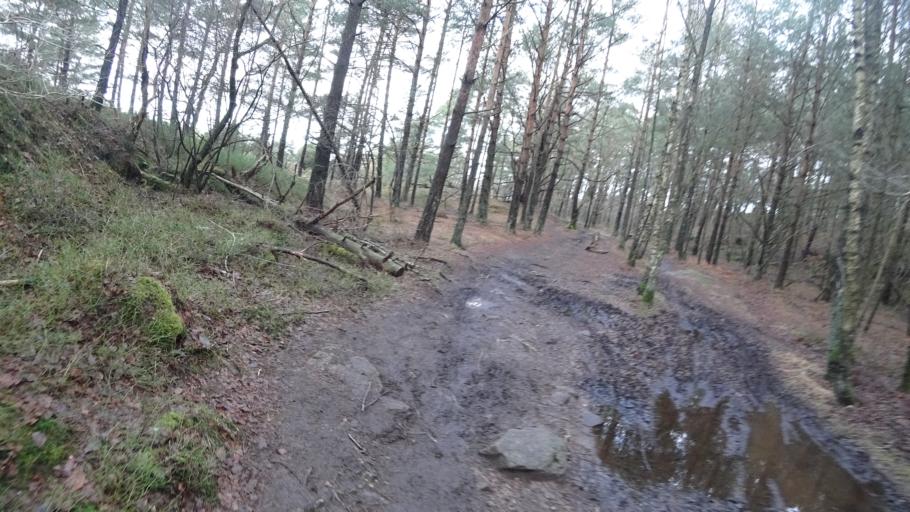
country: SE
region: Vaestra Goetaland
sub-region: Goteborg
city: Goeteborg
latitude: 57.6673
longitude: 11.9574
